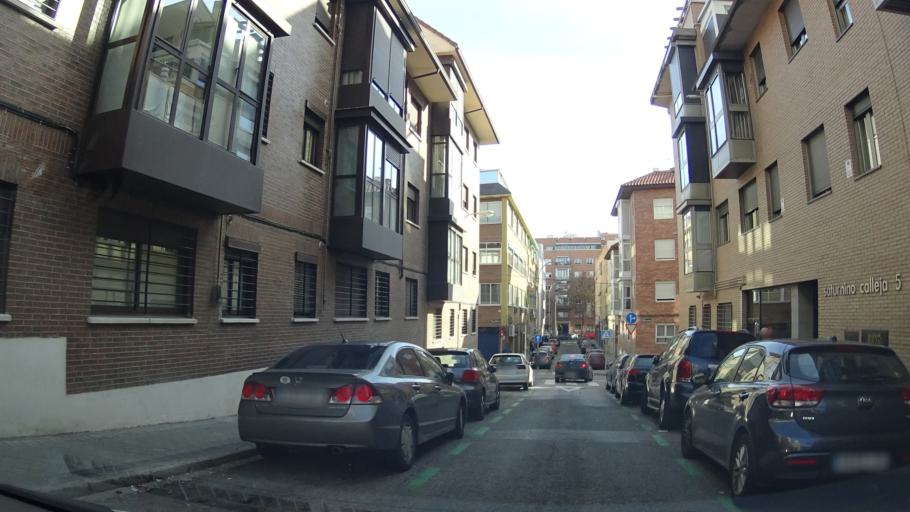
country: ES
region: Madrid
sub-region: Provincia de Madrid
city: Chamartin
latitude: 40.4487
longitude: -3.6696
